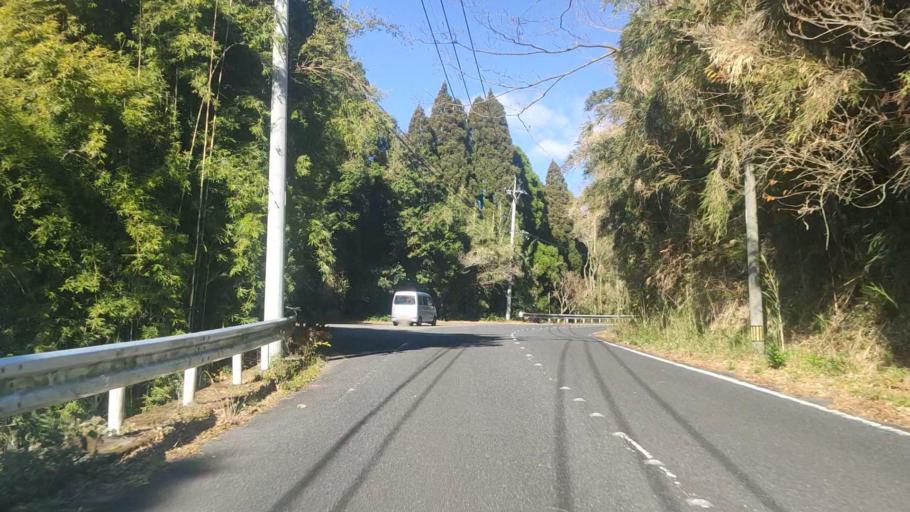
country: JP
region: Kagoshima
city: Kokubu-matsuki
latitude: 31.6708
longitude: 130.8303
